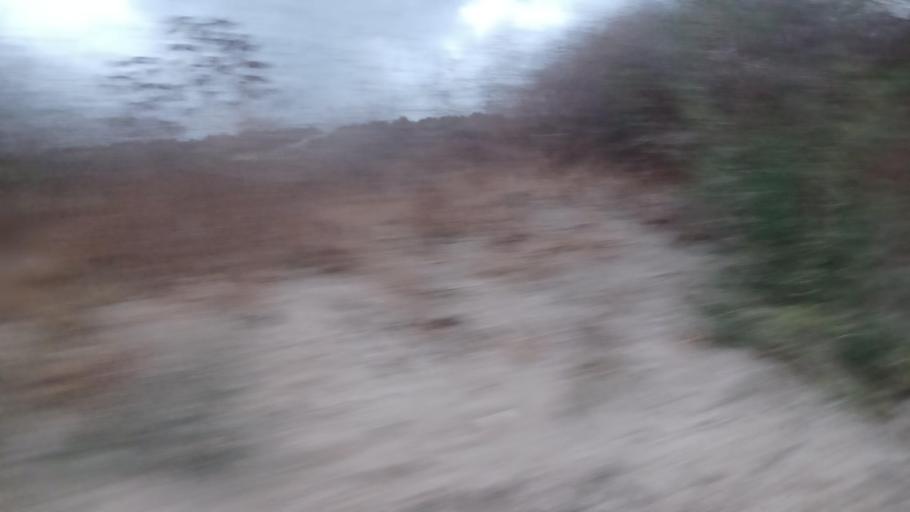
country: CY
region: Pafos
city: Mesogi
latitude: 34.8502
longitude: 32.5276
